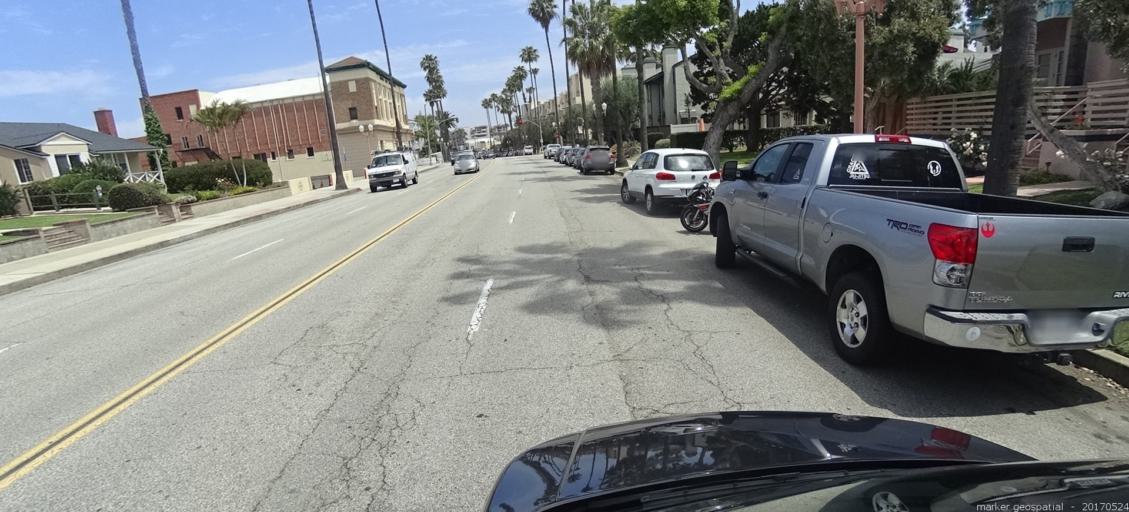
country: US
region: California
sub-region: Los Angeles County
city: Redondo Beach
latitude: 33.8342
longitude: -118.3879
